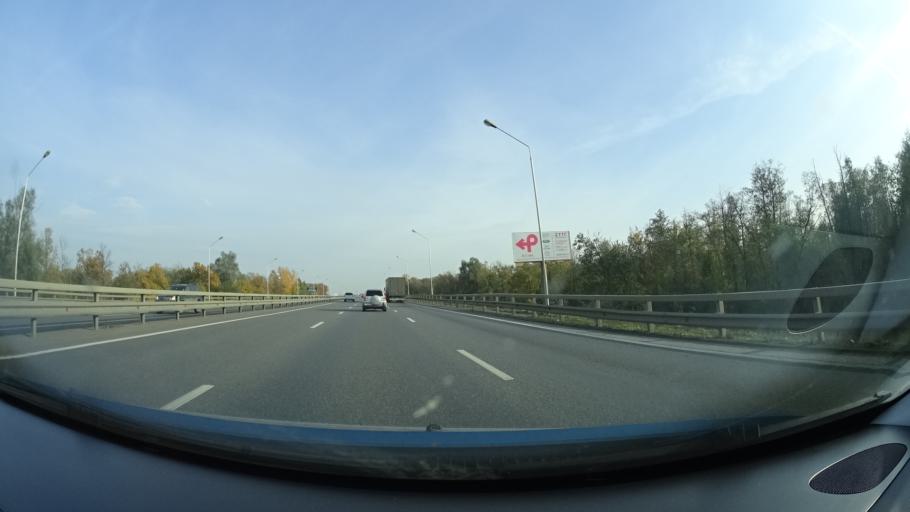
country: RU
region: Bashkortostan
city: Ufa
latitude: 54.6525
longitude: 55.9024
